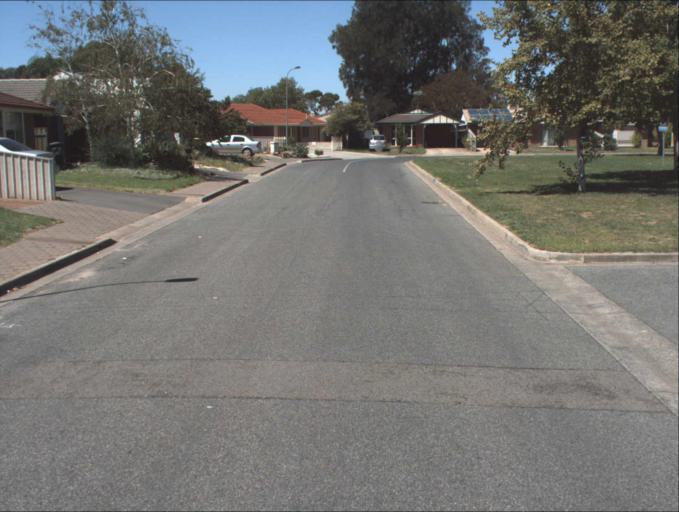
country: AU
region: South Australia
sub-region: Port Adelaide Enfield
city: Blair Athol
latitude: -34.8699
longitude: 138.6081
